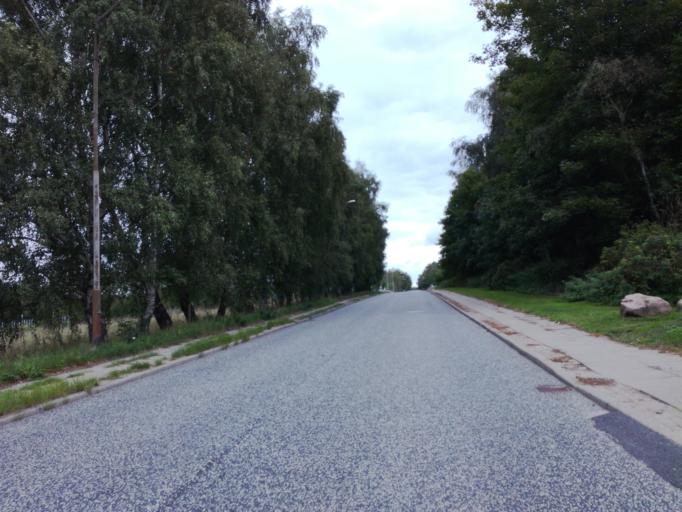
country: DK
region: South Denmark
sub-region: Vejle Kommune
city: Vejle
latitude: 55.6873
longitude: 9.5649
